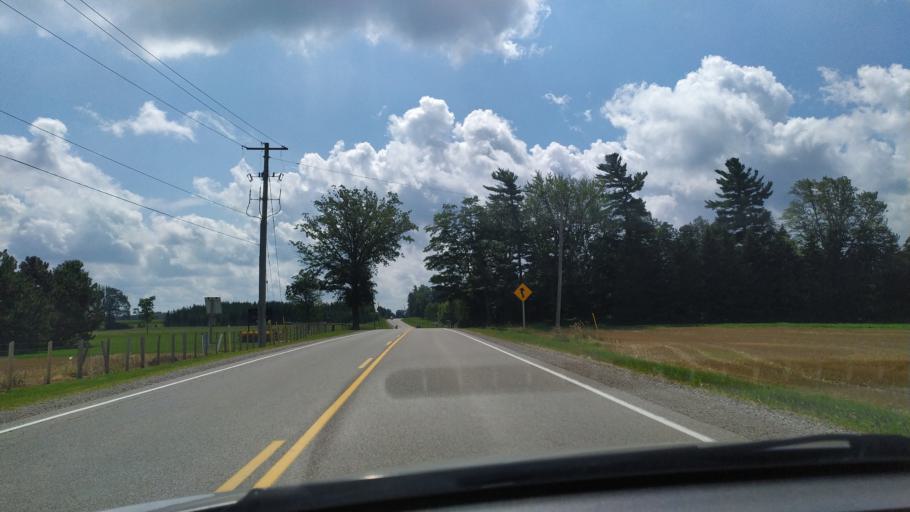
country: CA
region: Ontario
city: London
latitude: 43.0745
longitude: -81.3397
